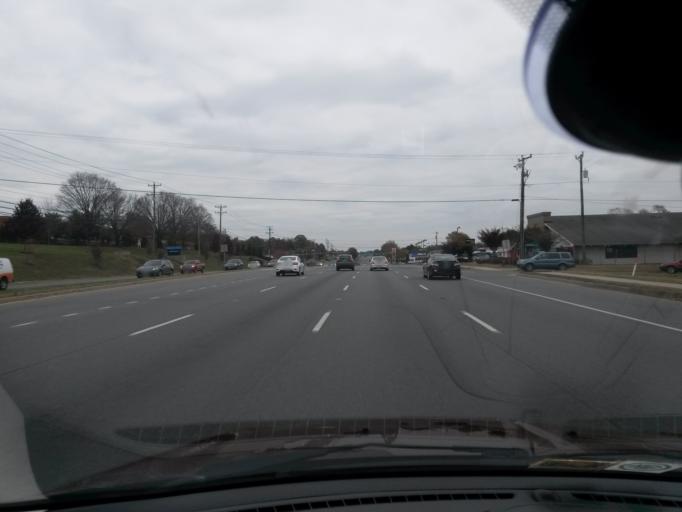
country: US
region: Virginia
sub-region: City of Charlottesville
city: Charlottesville
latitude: 38.0681
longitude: -78.4861
